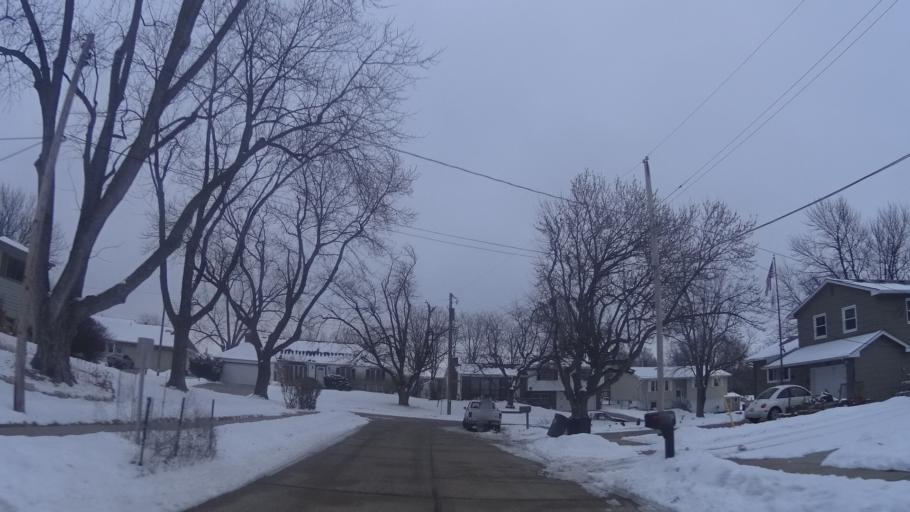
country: US
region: Nebraska
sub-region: Sarpy County
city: Offutt Air Force Base
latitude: 41.1502
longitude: -95.9224
